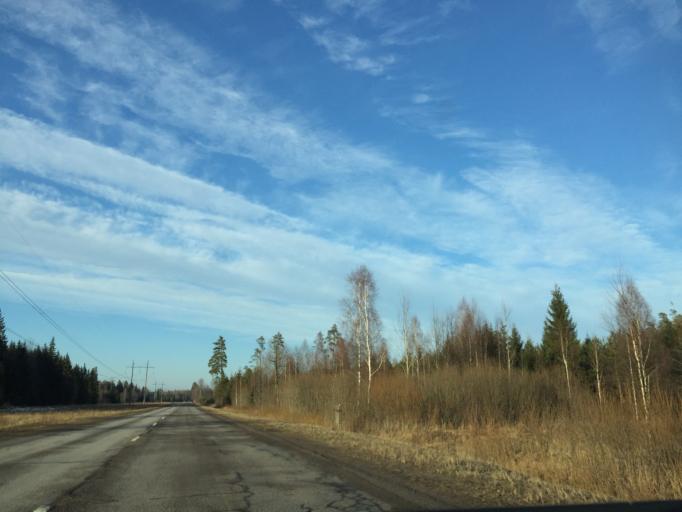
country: LV
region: Kekava
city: Balozi
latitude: 56.7910
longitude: 24.0758
